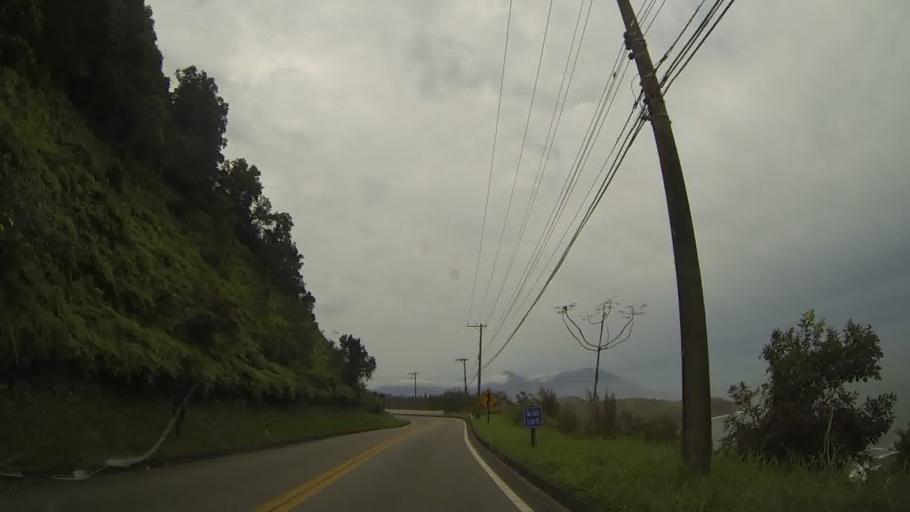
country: BR
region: Sao Paulo
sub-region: Sao Sebastiao
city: Sao Sebastiao
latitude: -23.8276
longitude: -45.5217
